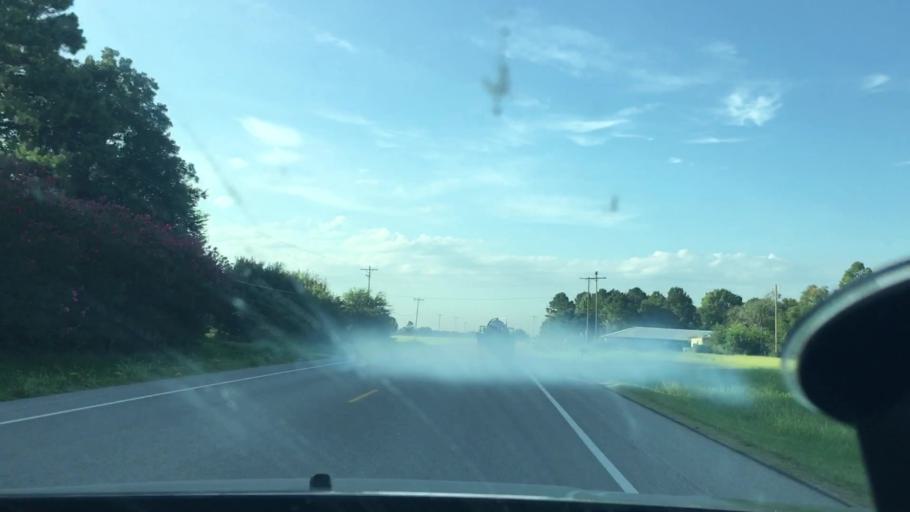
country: US
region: Oklahoma
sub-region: Garvin County
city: Wynnewood
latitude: 34.6673
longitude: -97.2052
